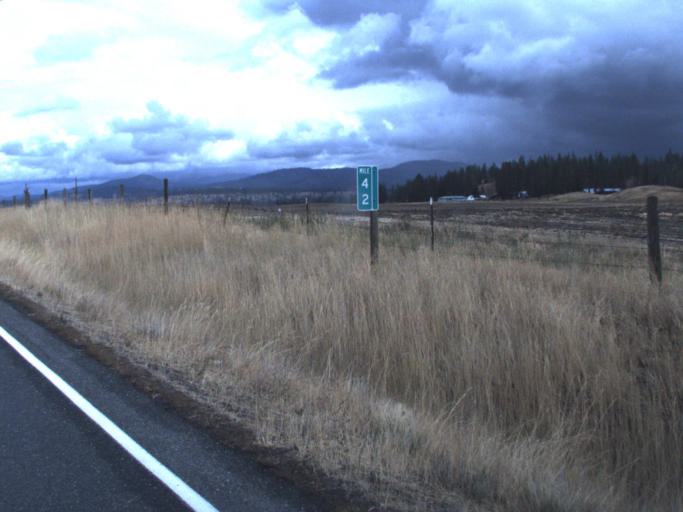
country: US
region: Washington
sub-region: Lincoln County
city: Davenport
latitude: 47.8175
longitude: -117.8871
